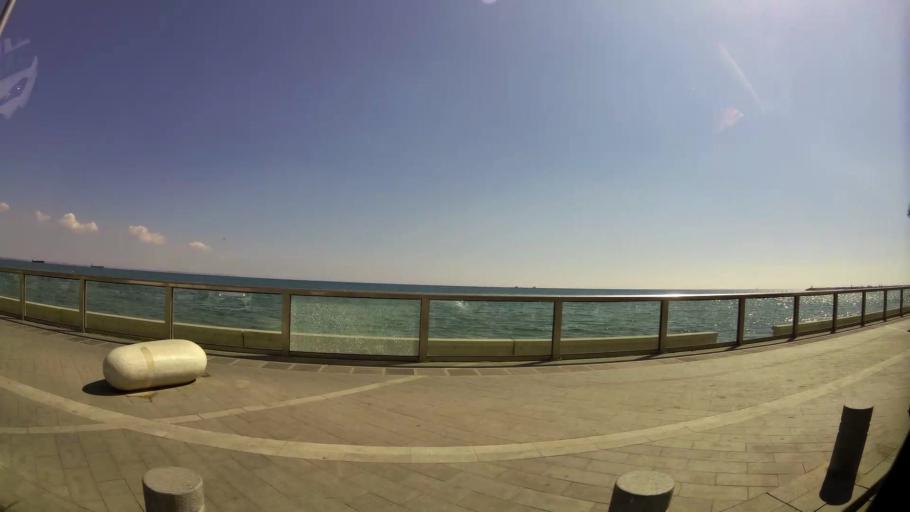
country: CY
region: Larnaka
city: Larnaca
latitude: 34.9041
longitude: 33.6377
